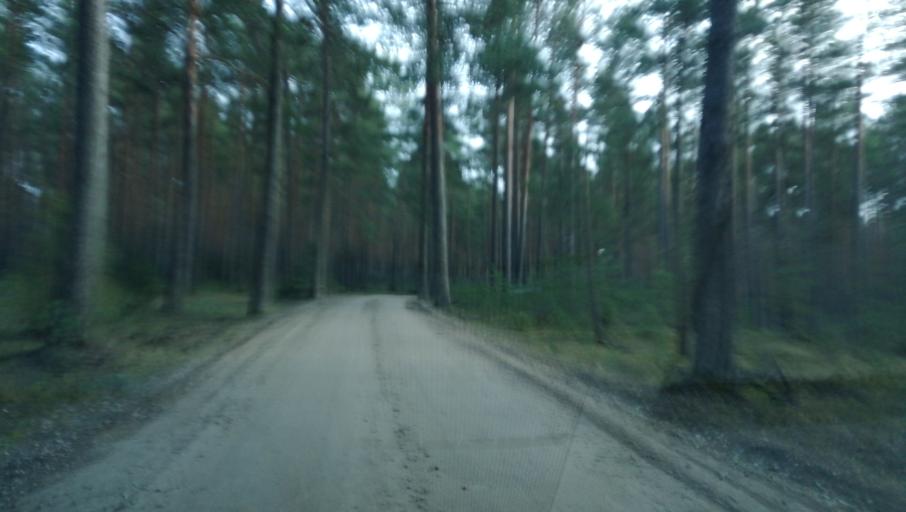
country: LV
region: Adazi
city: Adazi
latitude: 57.0556
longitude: 24.2996
